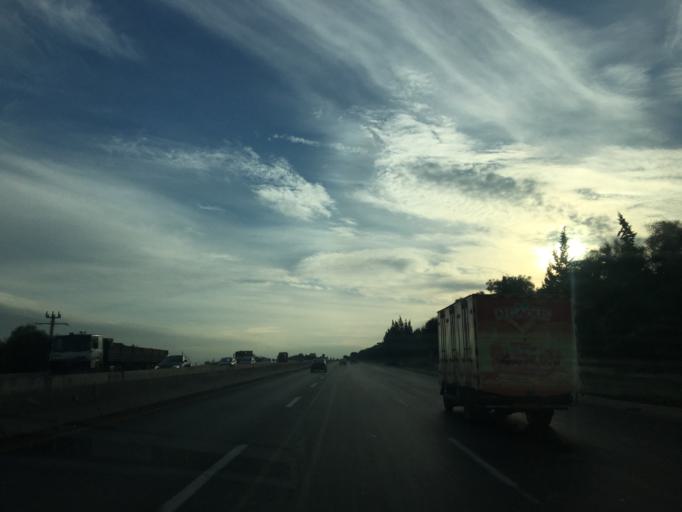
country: DZ
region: Bouira
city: Draa el Mizan
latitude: 36.4746
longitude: 3.7535
